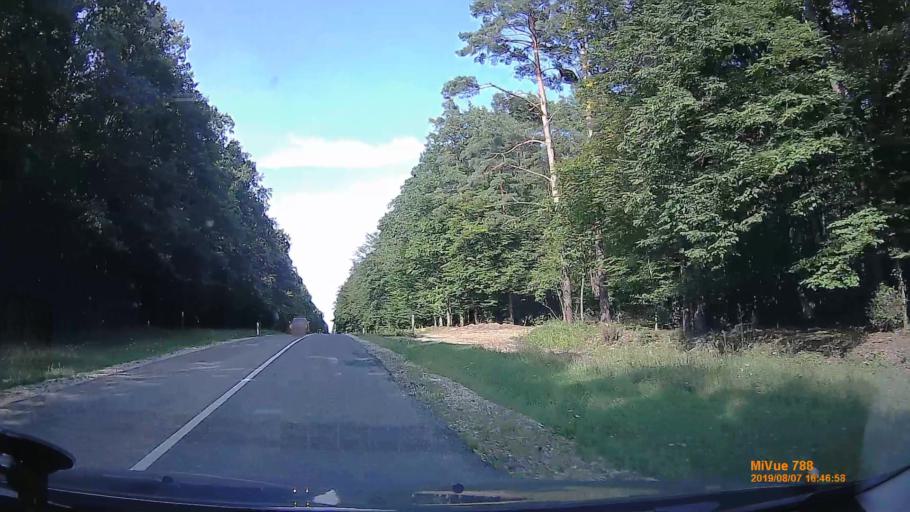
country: HU
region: Zala
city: Lenti
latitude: 46.6574
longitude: 16.6306
